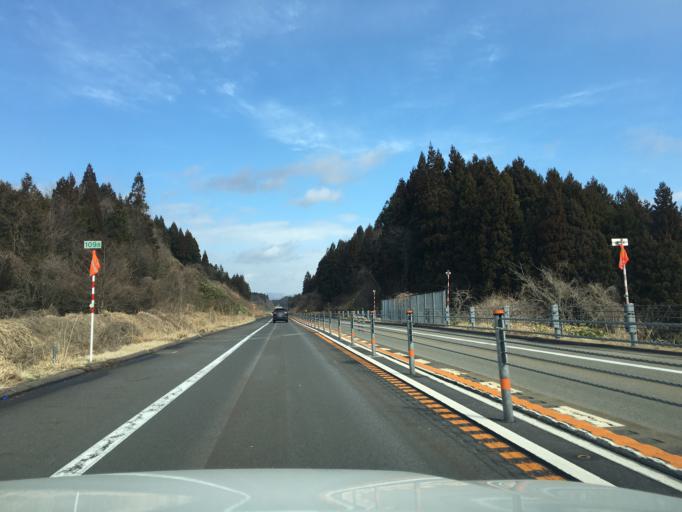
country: JP
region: Akita
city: Akita
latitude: 39.6872
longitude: 140.1857
